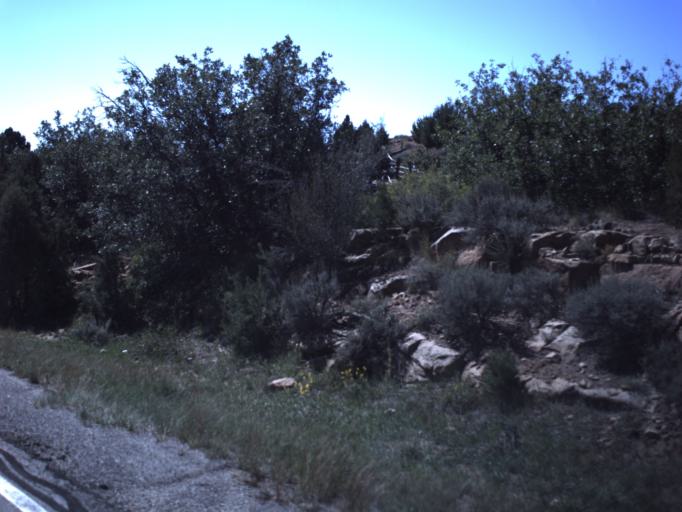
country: US
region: Utah
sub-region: Grand County
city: Moab
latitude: 38.3281
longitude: -109.2255
